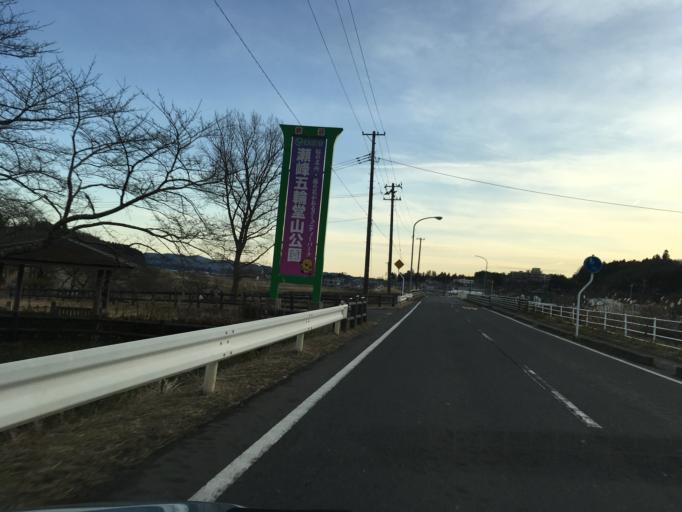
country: JP
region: Miyagi
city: Kogota
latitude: 38.6610
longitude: 141.0736
